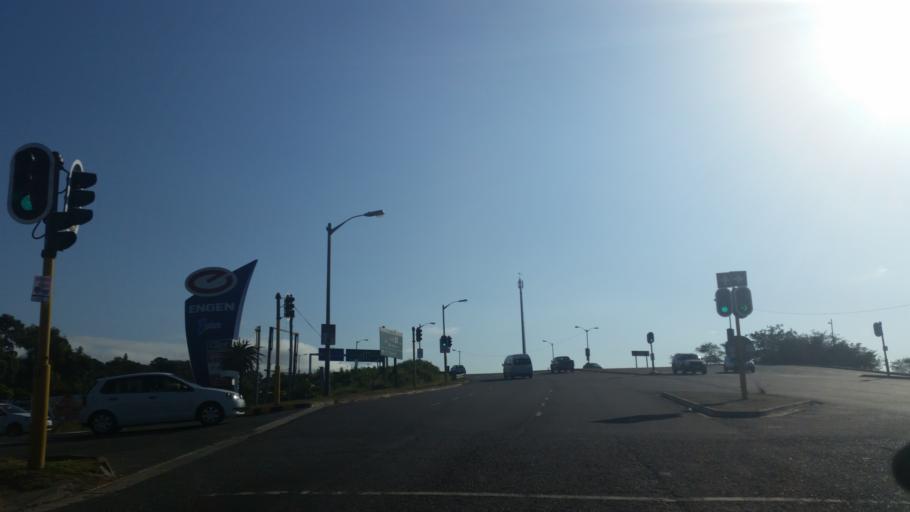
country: ZA
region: KwaZulu-Natal
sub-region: eThekwini Metropolitan Municipality
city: Berea
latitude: -29.8505
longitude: 30.9316
